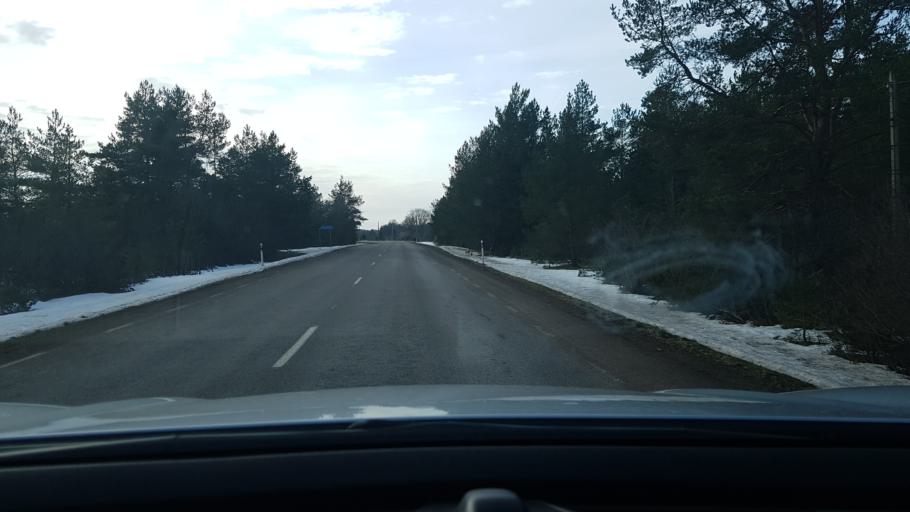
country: EE
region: Saare
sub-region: Kuressaare linn
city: Kuressaare
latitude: 58.3207
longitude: 22.5490
